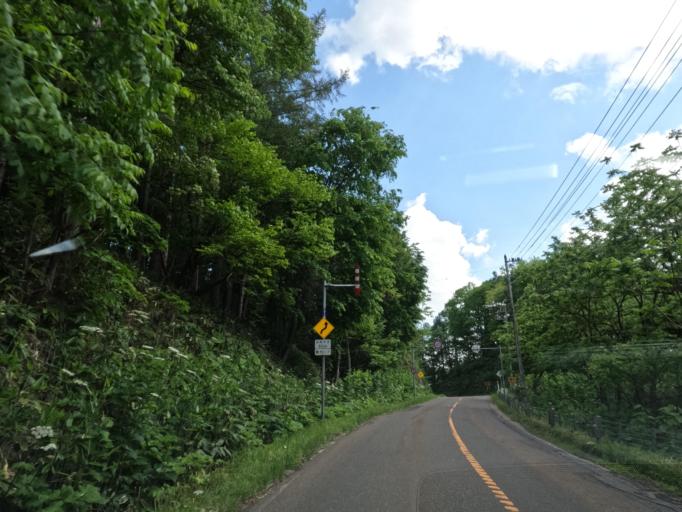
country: JP
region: Hokkaido
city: Takikawa
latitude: 43.5769
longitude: 141.8350
